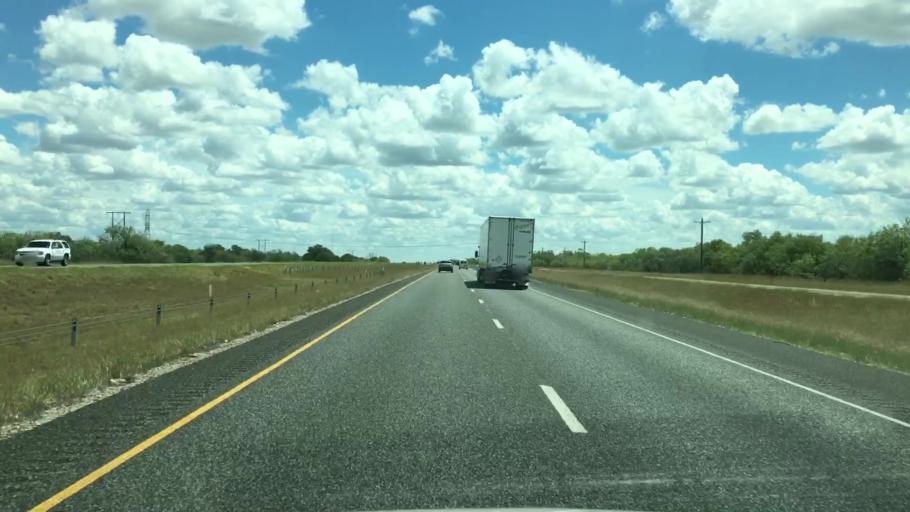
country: US
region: Texas
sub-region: Atascosa County
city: Pleasanton
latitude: 28.8275
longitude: -98.3670
